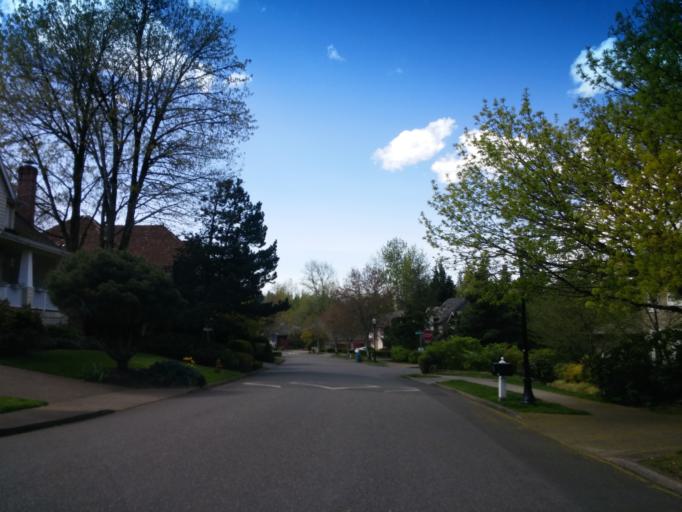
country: US
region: Oregon
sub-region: Washington County
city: West Haven
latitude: 45.5357
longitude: -122.7794
